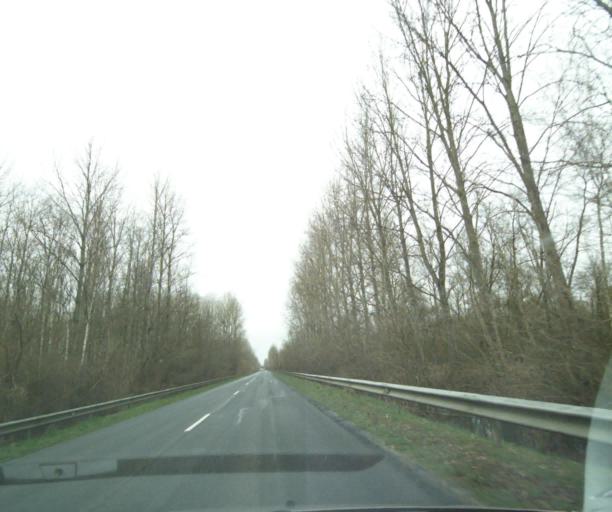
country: FR
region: Picardie
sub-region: Departement de l'Oise
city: Noyon
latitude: 49.5590
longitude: 3.0382
